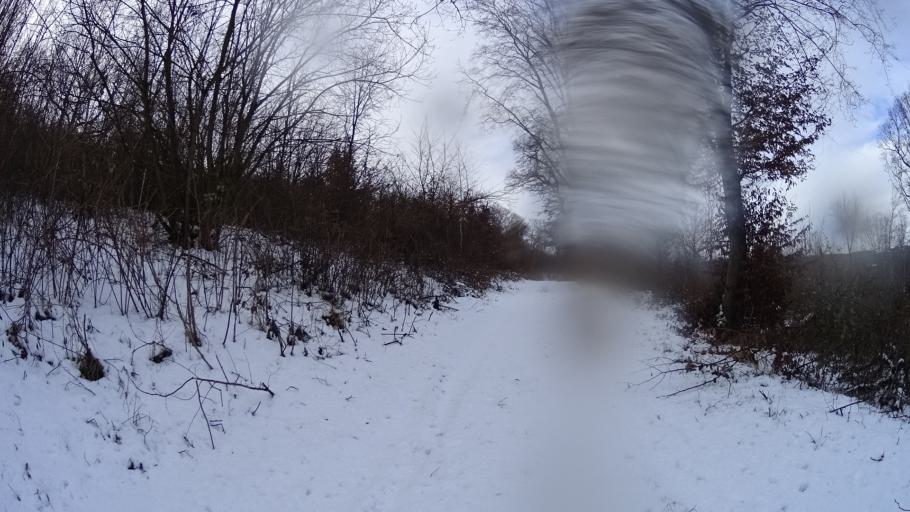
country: AT
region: Lower Austria
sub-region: Politischer Bezirk Korneuburg
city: Leobendorf
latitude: 48.4069
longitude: 16.3282
